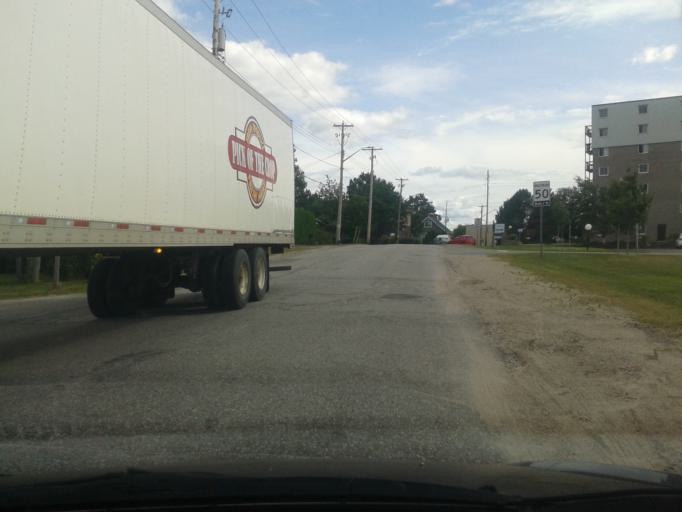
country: CA
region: Ontario
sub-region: Nipissing District
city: North Bay
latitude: 46.3346
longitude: -79.4633
